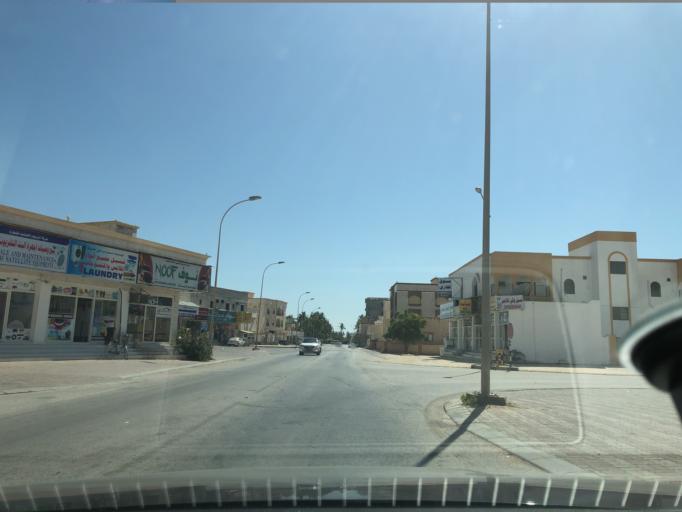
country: OM
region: Zufar
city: Salalah
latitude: 17.0210
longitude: 54.1567
